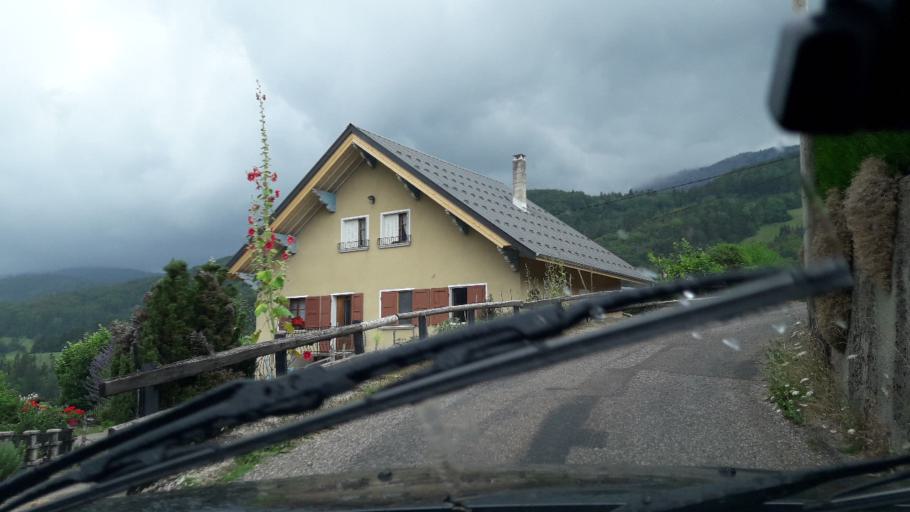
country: FR
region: Rhone-Alpes
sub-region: Departement de la Savoie
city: Vimines
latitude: 45.4680
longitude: 5.8848
